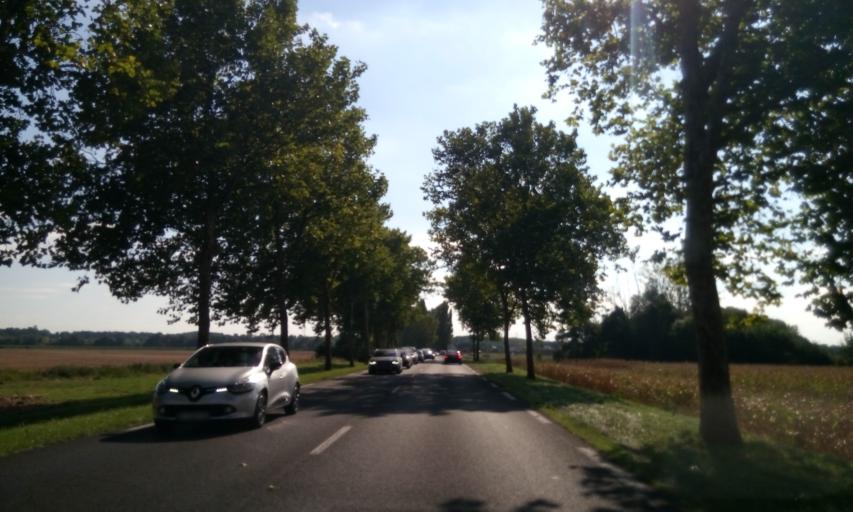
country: FR
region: Centre
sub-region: Departement d'Indre-et-Loire
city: Poce-sur-Cisse
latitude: 47.4419
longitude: 1.0078
